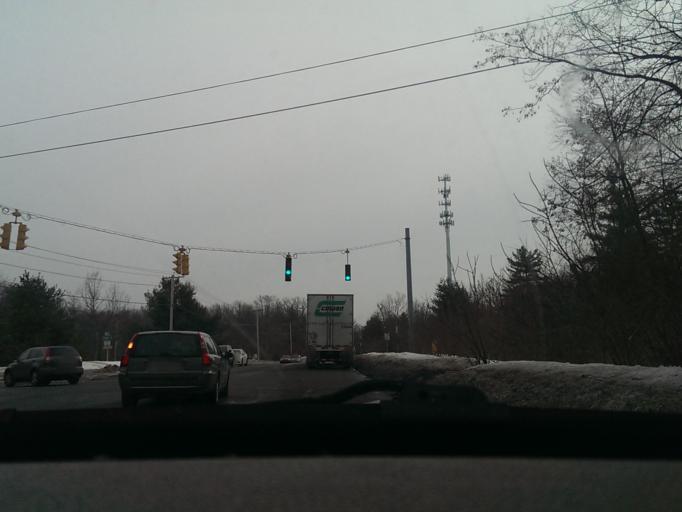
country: US
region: Massachusetts
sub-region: Hampden County
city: East Longmeadow
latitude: 42.0569
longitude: -72.5356
